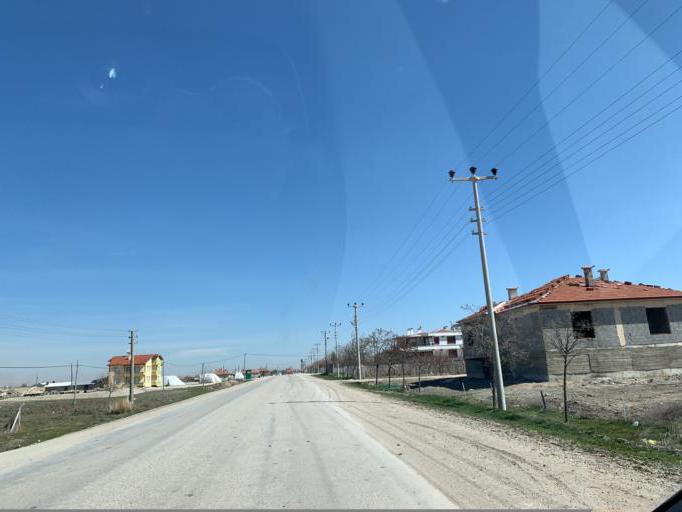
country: TR
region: Konya
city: Yarma
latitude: 37.7498
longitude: 32.8457
